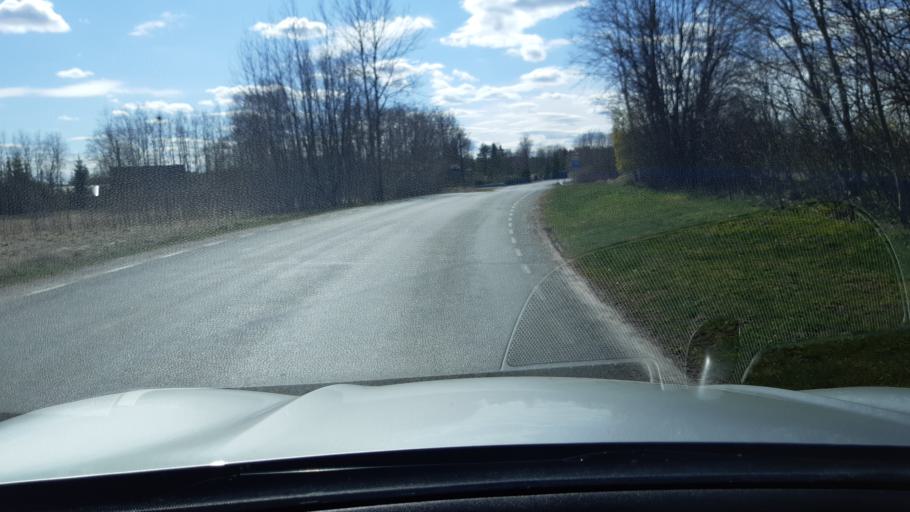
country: EE
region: Raplamaa
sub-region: Kohila vald
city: Kohila
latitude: 59.1786
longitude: 24.8518
